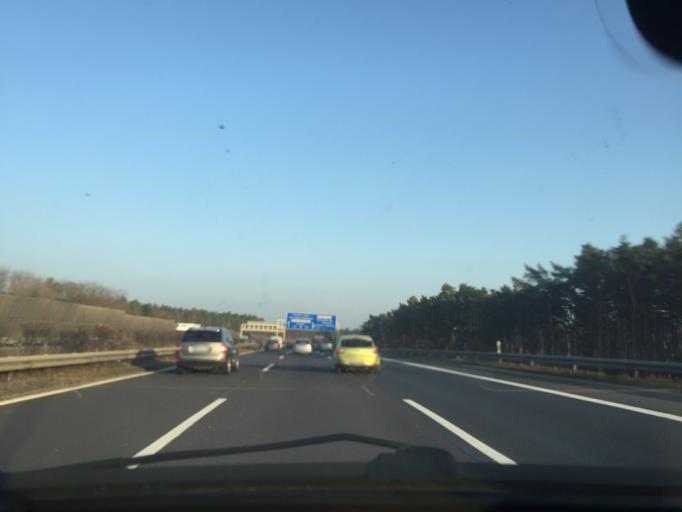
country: DE
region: Brandenburg
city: Michendorf
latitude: 52.2991
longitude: 13.0400
